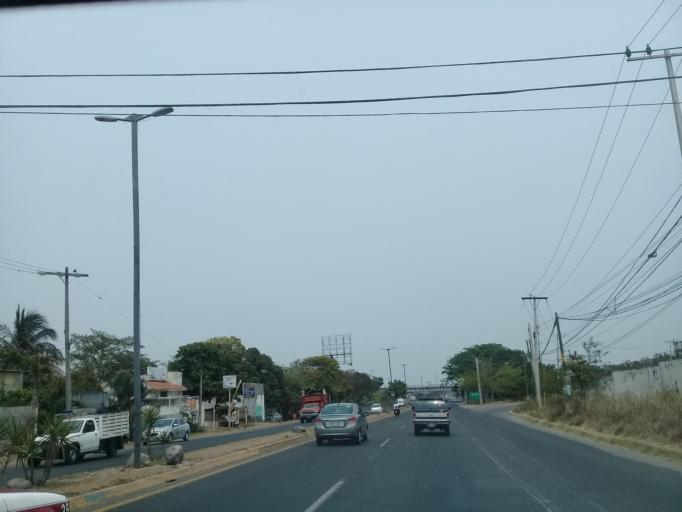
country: MX
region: Veracruz
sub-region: Veracruz
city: Hacienda Sotavento
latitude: 19.1510
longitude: -96.1770
